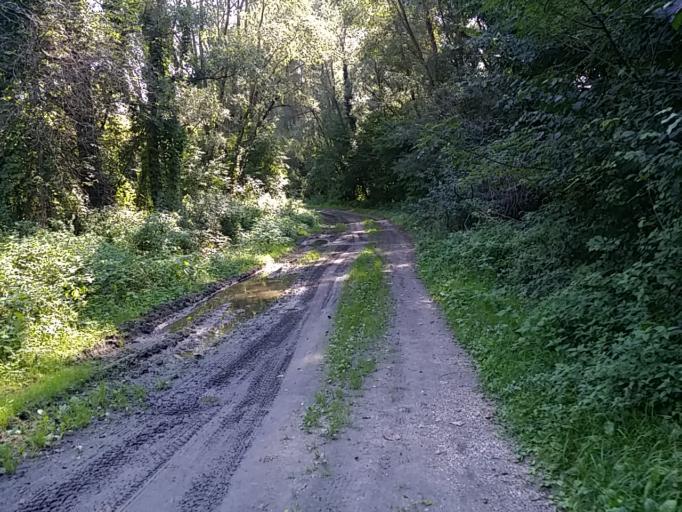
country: HR
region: Koprivnicko-Krizevacka
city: Ferdinandovac
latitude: 46.1202
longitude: 17.2004
